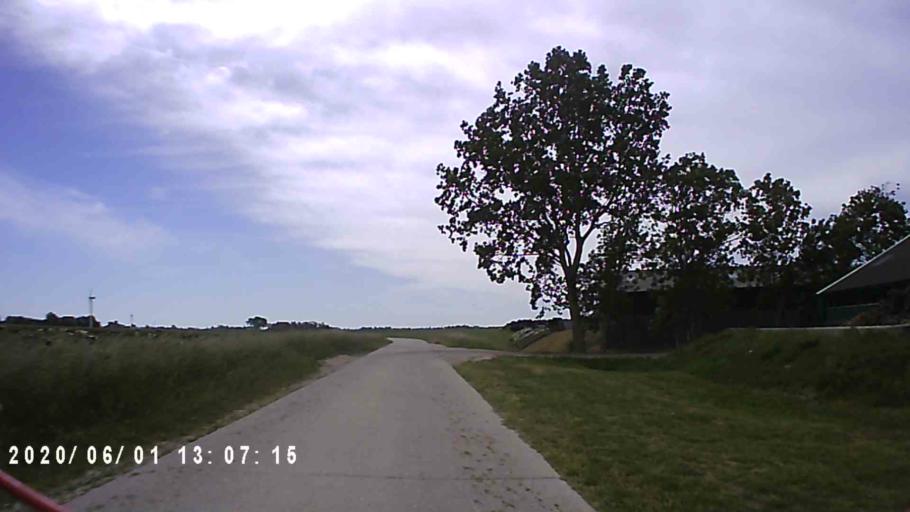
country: NL
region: Friesland
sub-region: Gemeente Franekeradeel
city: Tzum
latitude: 53.1325
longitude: 5.5543
